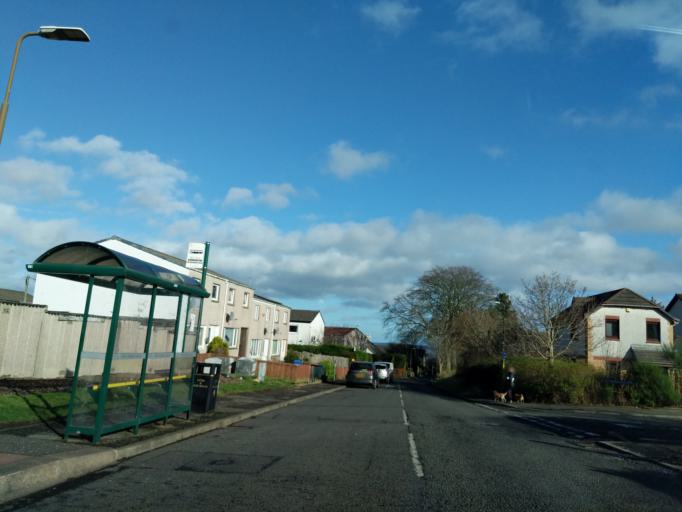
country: GB
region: Scotland
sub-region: West Lothian
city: Kirknewton
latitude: 55.8893
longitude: -3.4144
